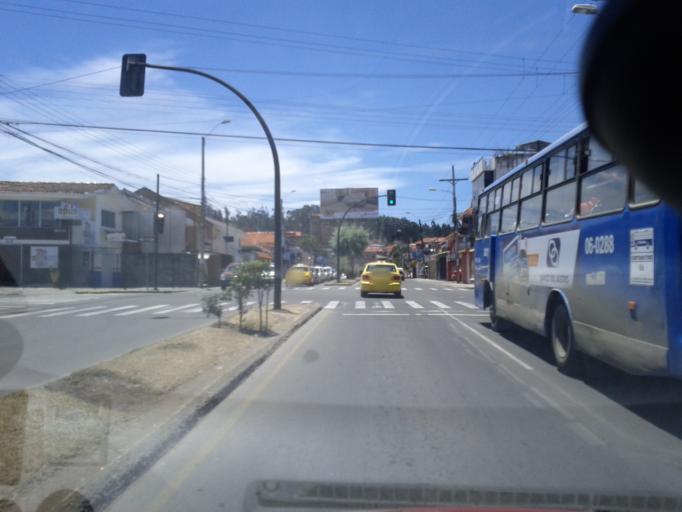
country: EC
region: Azuay
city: Cuenca
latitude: -2.8969
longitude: -79.0195
